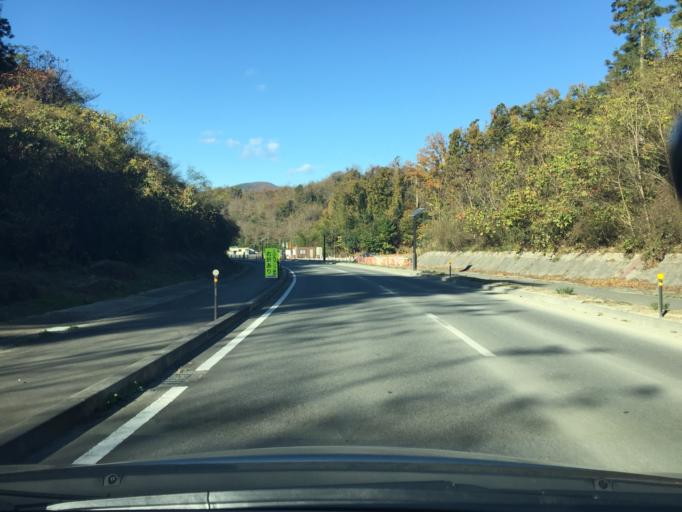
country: JP
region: Fukushima
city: Iwaki
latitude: 37.0124
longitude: 140.8591
